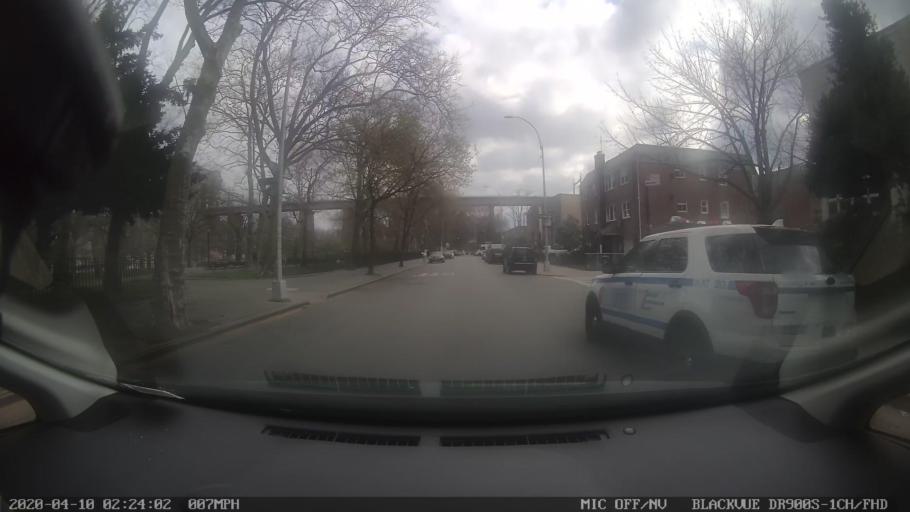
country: US
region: New York
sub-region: Queens County
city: Long Island City
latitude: 40.7791
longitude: -73.9206
